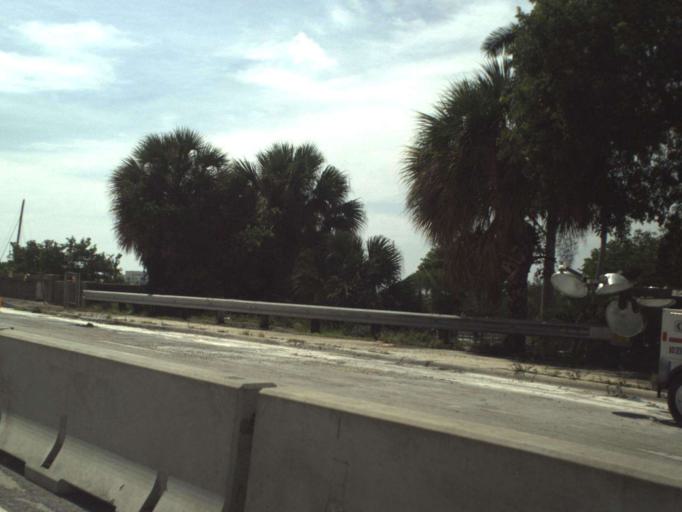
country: US
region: Florida
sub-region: Palm Beach County
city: West Palm Beach
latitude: 26.7185
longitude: -80.0508
